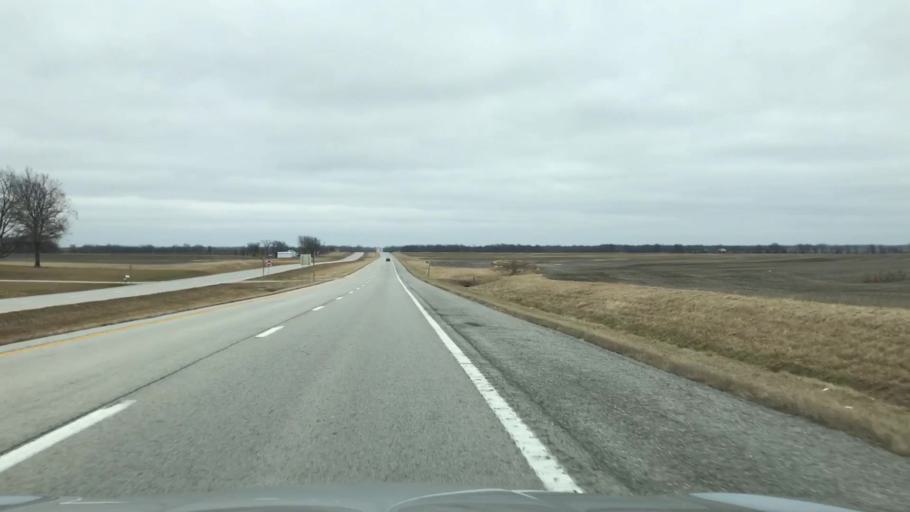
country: US
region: Missouri
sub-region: Livingston County
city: Chillicothe
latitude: 39.7761
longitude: -93.4715
